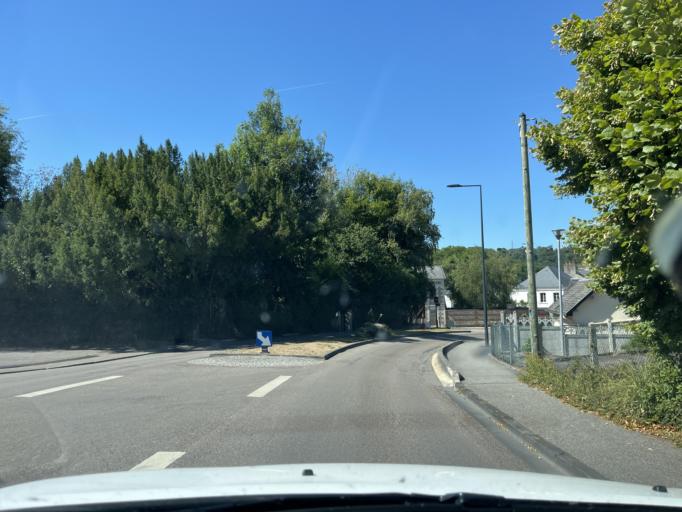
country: FR
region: Haute-Normandie
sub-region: Departement de la Seine-Maritime
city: Lillebonne
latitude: 49.5181
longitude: 0.5429
